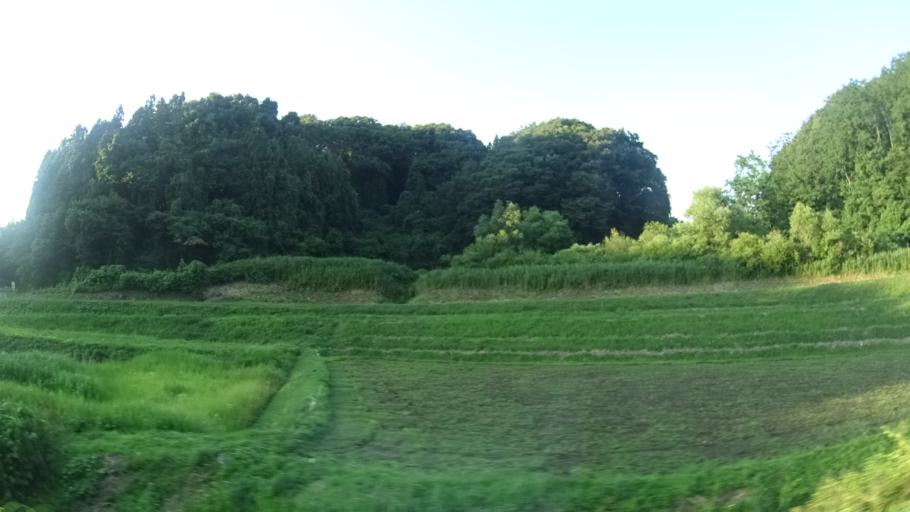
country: JP
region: Fukushima
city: Miharu
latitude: 37.4575
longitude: 140.5112
